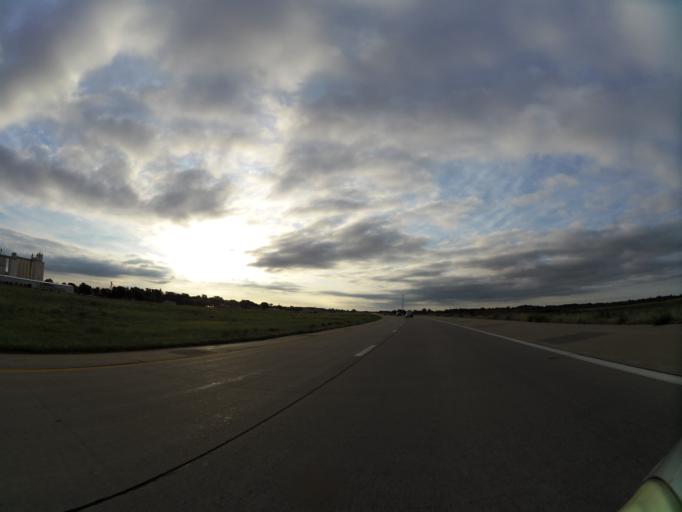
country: US
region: Kansas
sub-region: Reno County
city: Haven
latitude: 37.8962
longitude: -97.7881
